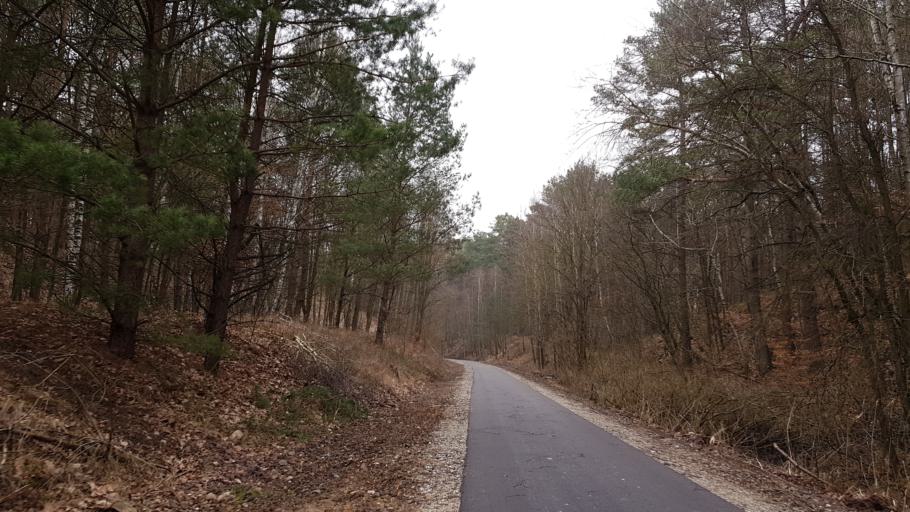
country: PL
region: West Pomeranian Voivodeship
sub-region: Powiat mysliborski
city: Barlinek
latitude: 53.0046
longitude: 15.2419
